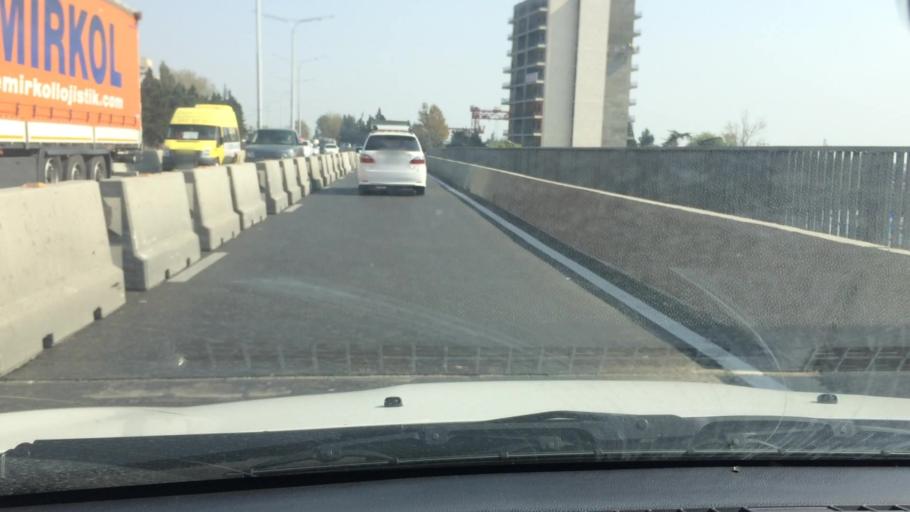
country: GE
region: T'bilisi
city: Tbilisi
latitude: 41.6842
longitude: 44.8699
